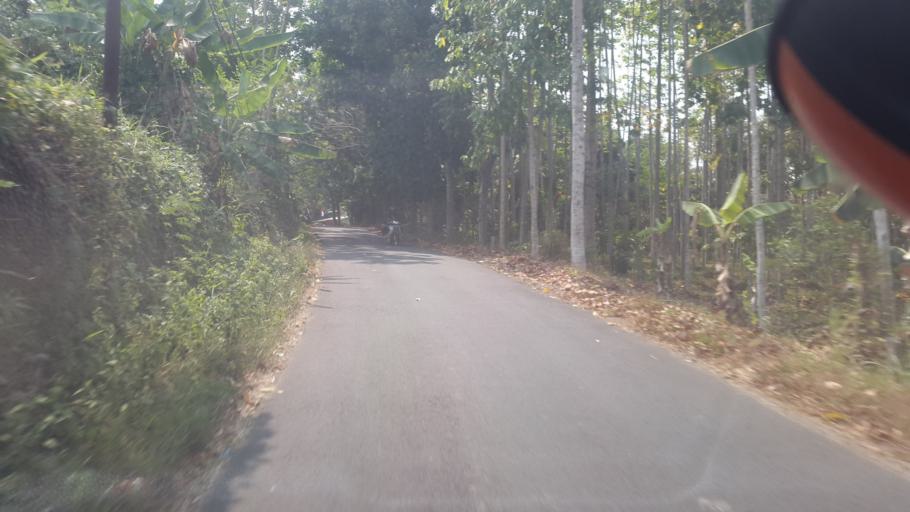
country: ID
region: West Java
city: Cimaja
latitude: -6.9484
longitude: 106.5069
